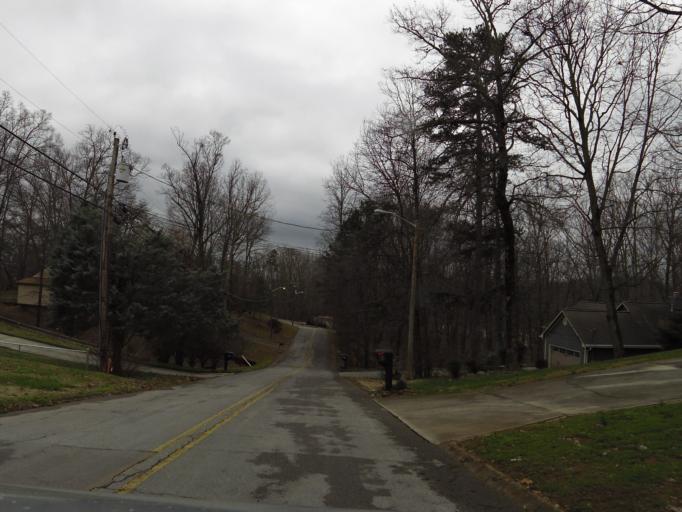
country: US
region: Tennessee
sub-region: Knox County
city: Knoxville
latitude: 35.9900
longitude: -84.0321
